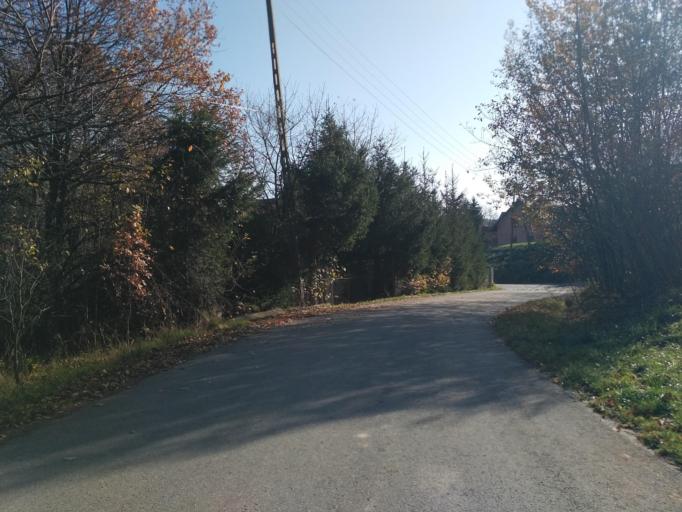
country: PL
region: Subcarpathian Voivodeship
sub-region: Powiat rzeszowski
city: Blazowa
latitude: 49.8606
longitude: 22.1268
